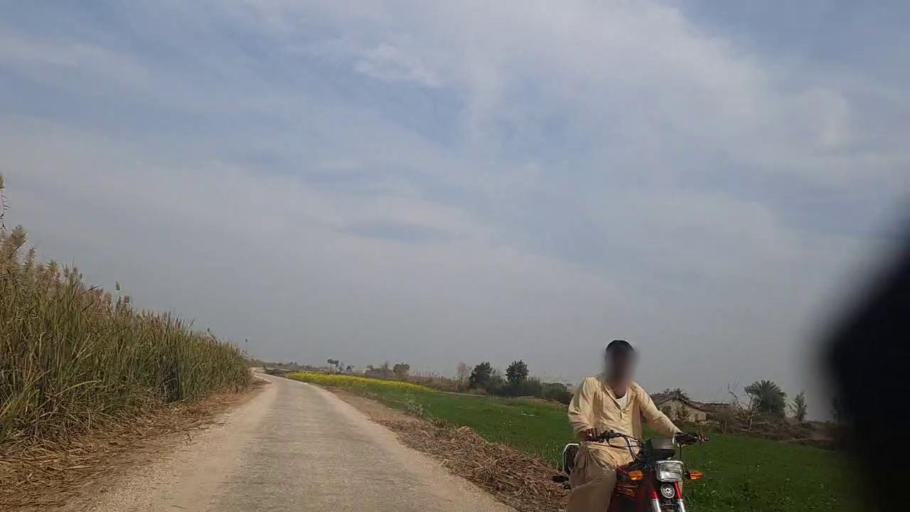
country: PK
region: Sindh
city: Daur
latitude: 26.3751
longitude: 68.2536
